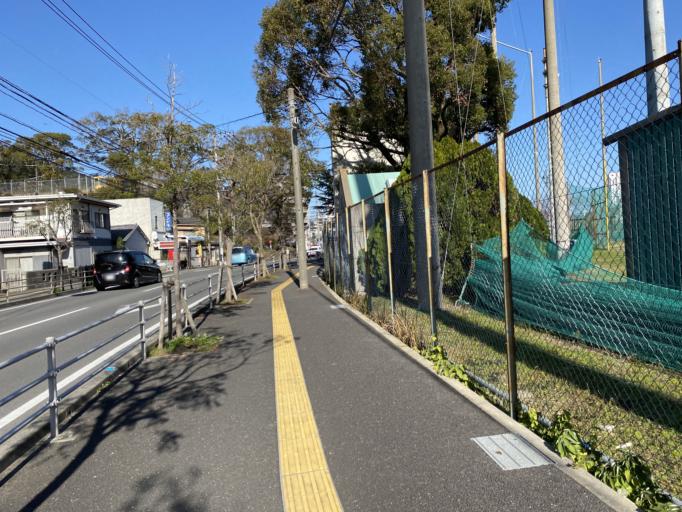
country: JP
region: Nagasaki
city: Nagasaki-shi
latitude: 32.7576
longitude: 129.8611
